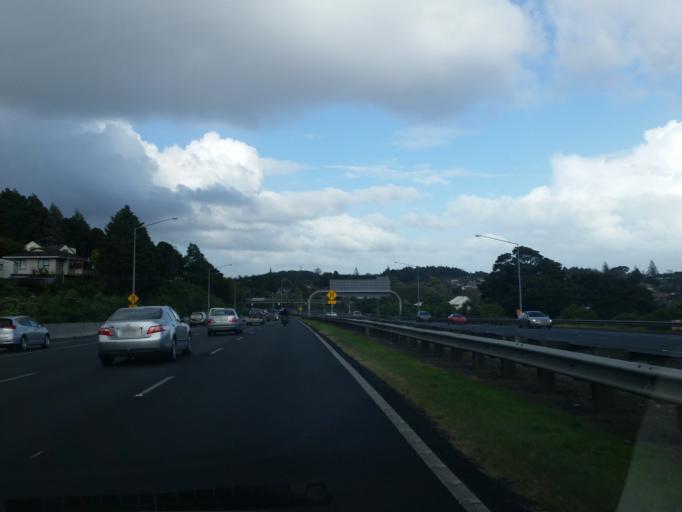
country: NZ
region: Auckland
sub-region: Auckland
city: Manukau City
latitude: -37.0030
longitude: 174.8950
